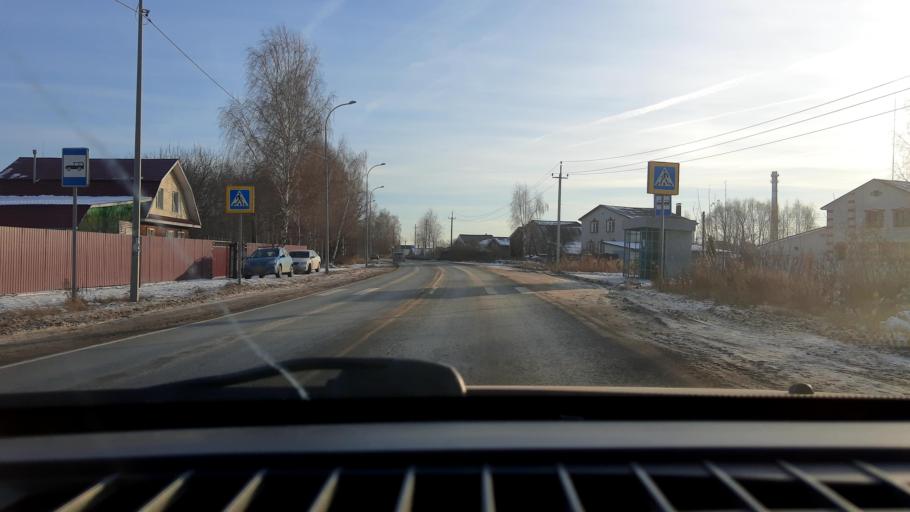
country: RU
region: Nizjnij Novgorod
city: Bor
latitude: 56.3798
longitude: 44.0428
